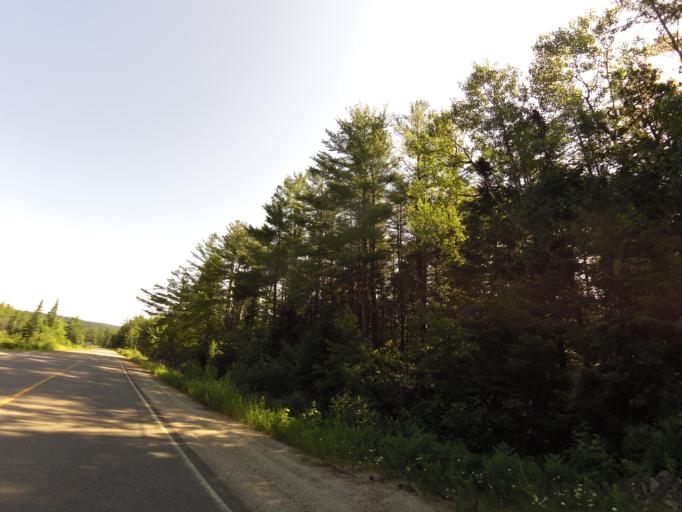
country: CA
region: Ontario
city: Deep River
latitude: 46.1819
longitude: -77.6808
